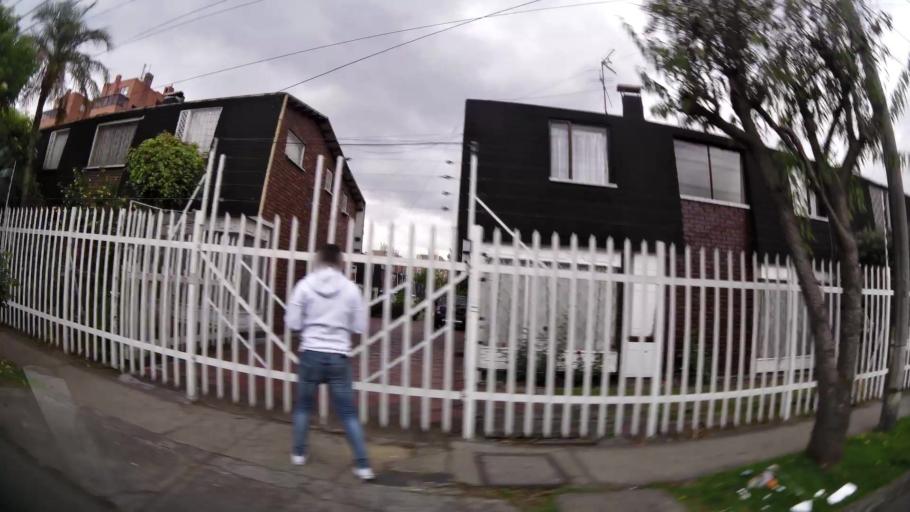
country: CO
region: Bogota D.C.
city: Bogota
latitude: 4.6619
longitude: -74.1176
